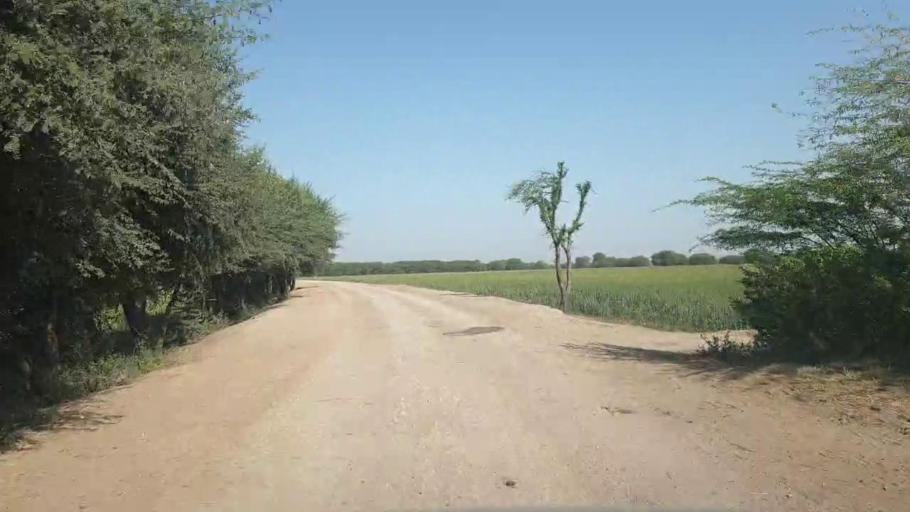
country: PK
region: Sindh
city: Umarkot
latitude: 25.3001
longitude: 69.6544
